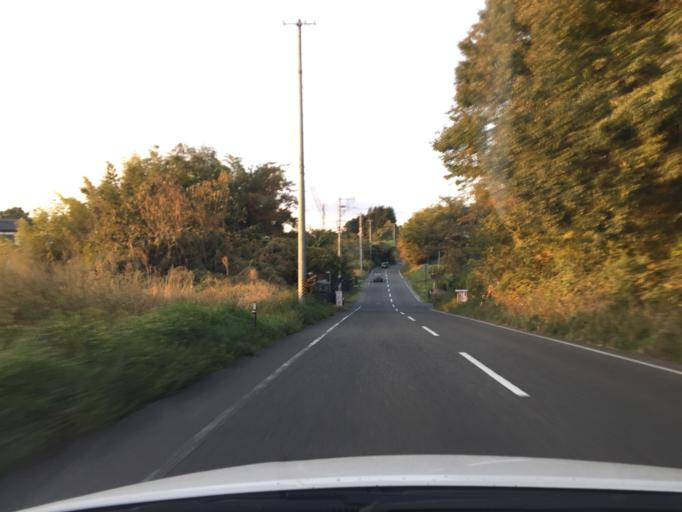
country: JP
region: Fukushima
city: Koriyama
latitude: 37.3612
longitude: 140.4481
